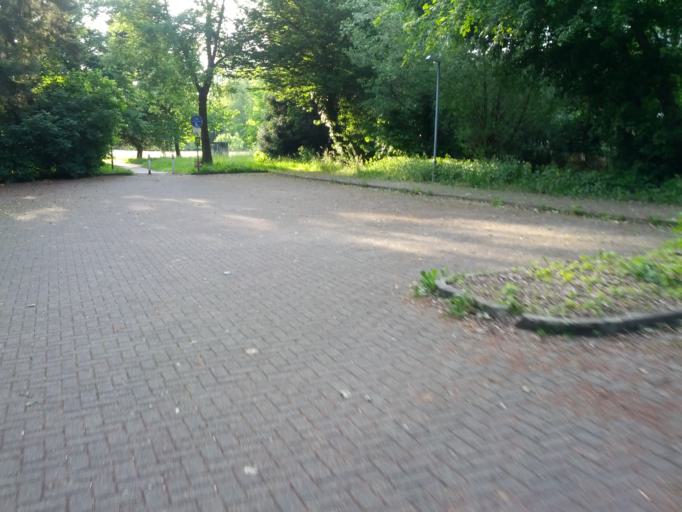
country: DE
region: Baden-Wuerttemberg
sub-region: Freiburg Region
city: Umkirch
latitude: 48.0289
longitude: 7.7656
